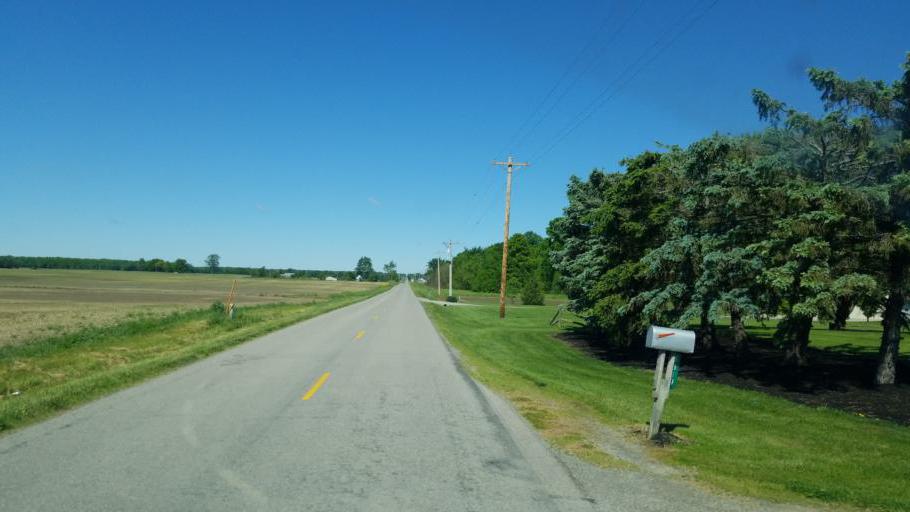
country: US
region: Ohio
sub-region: Logan County
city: Northwood
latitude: 40.4509
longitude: -83.5800
